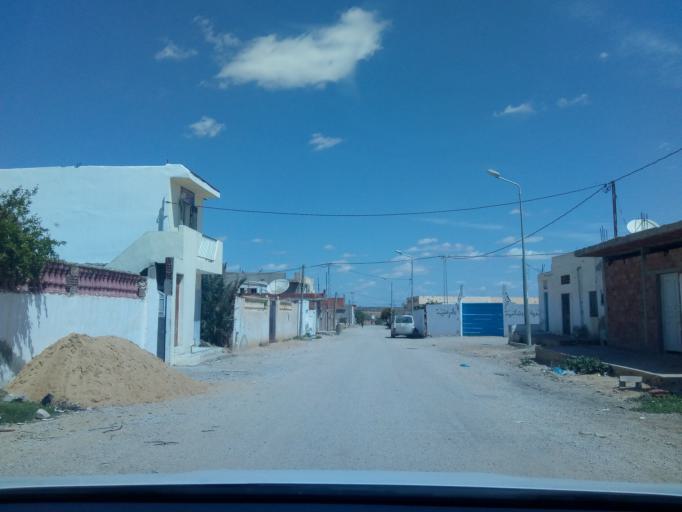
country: TN
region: Safaqis
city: Sfax
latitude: 34.7289
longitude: 10.4914
